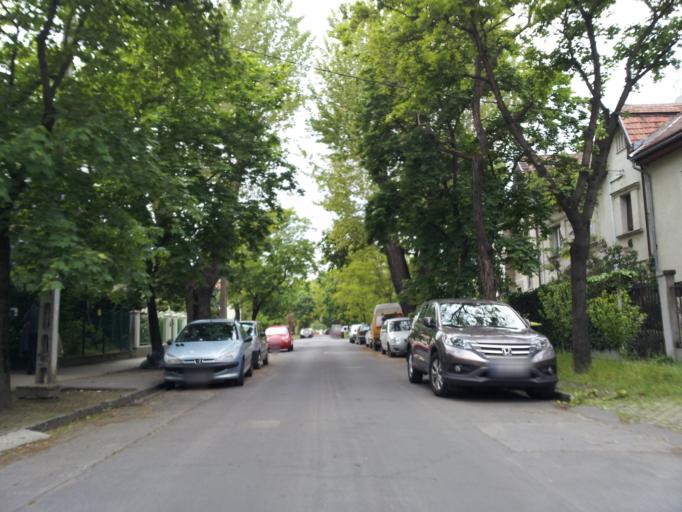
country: HU
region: Budapest
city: Budapest XIV. keruelet
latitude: 47.5249
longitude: 19.1087
